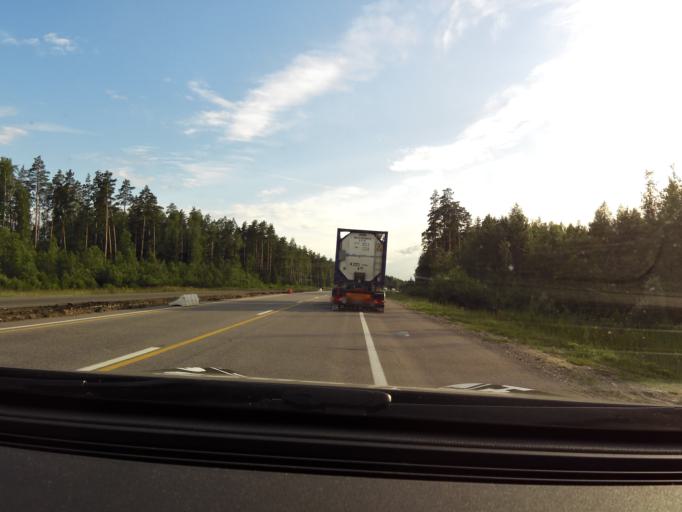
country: RU
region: Vladimir
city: Sudogda
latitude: 56.1168
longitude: 40.8481
